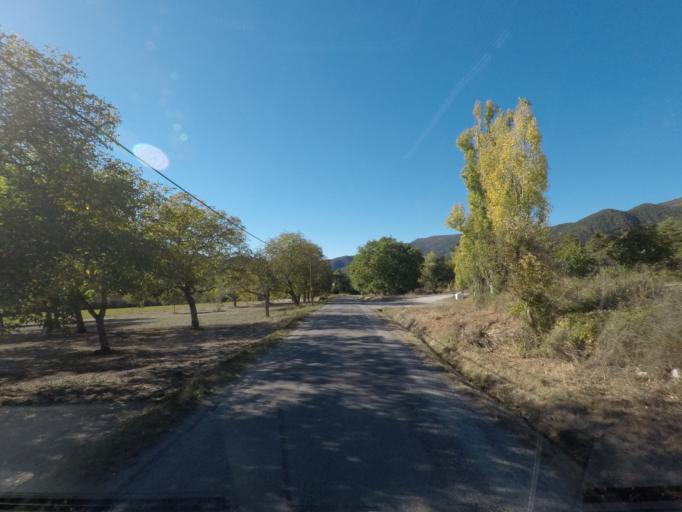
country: FR
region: Provence-Alpes-Cote d'Azur
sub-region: Departement des Hautes-Alpes
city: Serres
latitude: 44.4601
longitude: 5.5261
